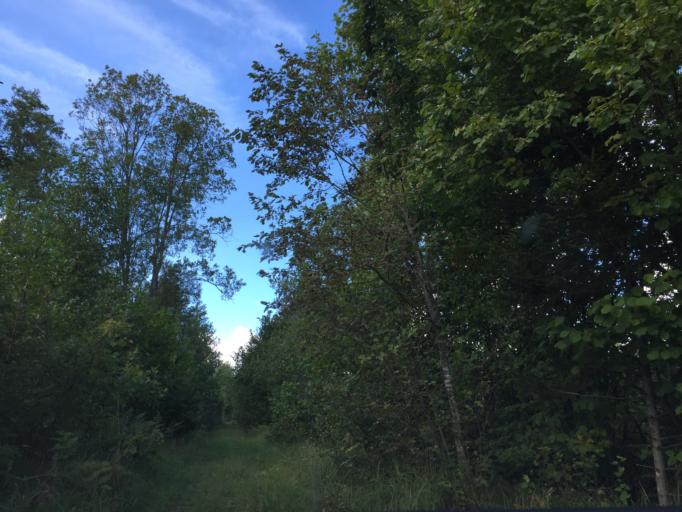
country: LV
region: Kuldigas Rajons
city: Kuldiga
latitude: 56.9790
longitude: 21.9010
